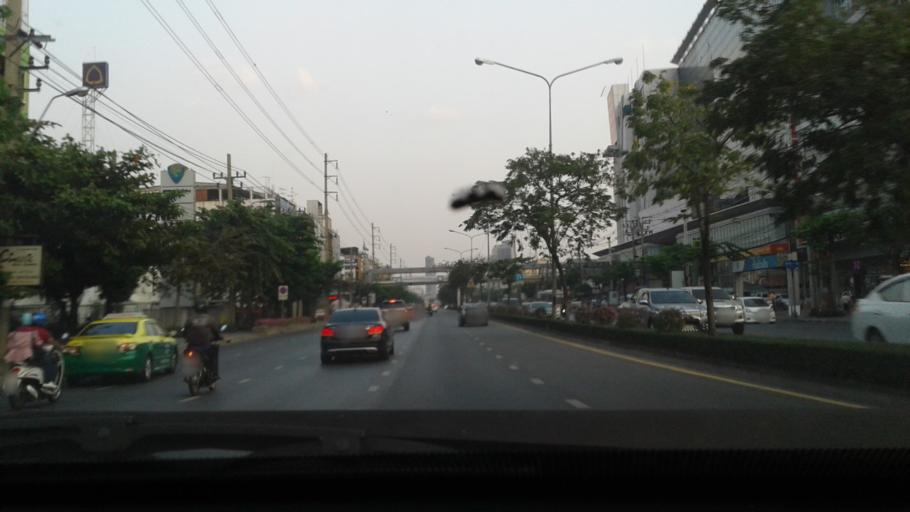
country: TH
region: Nonthaburi
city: Bang Kruai
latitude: 13.7890
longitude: 100.4820
